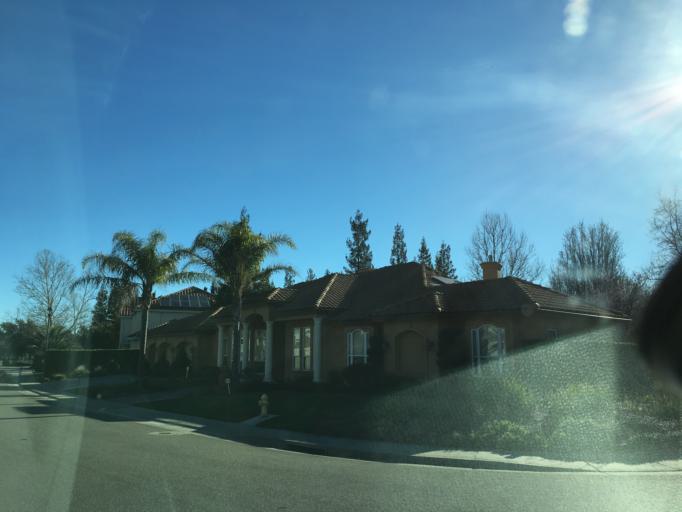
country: US
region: California
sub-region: Yolo County
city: Davis
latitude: 38.5595
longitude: -121.7074
